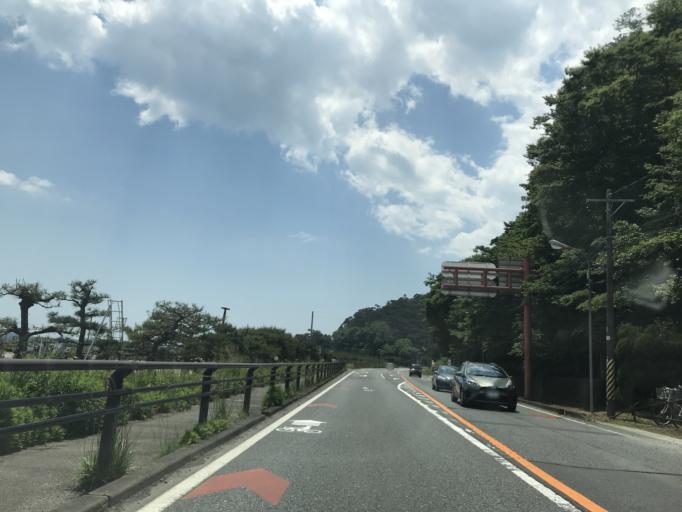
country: JP
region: Miyagi
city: Matsushima
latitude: 38.3646
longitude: 141.0604
